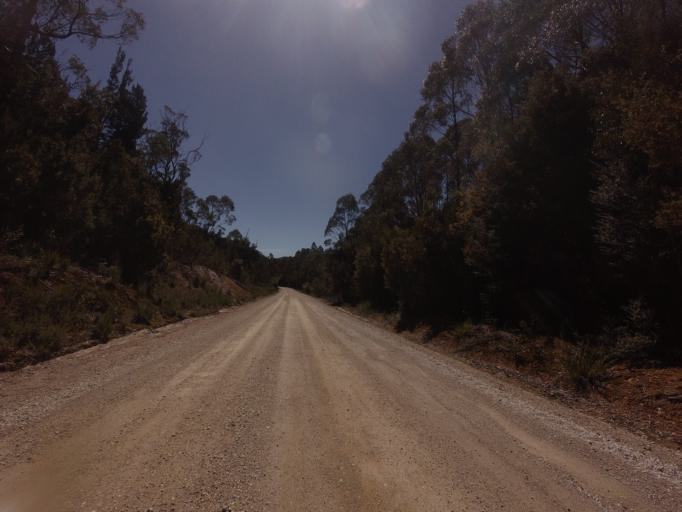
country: AU
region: Tasmania
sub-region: Huon Valley
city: Geeveston
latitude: -42.8245
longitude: 146.3894
